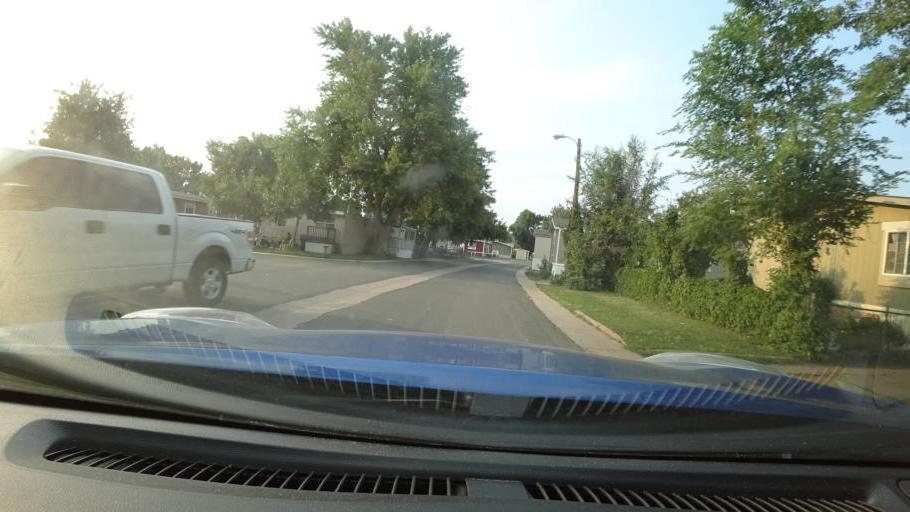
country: US
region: Colorado
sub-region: Adams County
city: Aurora
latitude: 39.7452
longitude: -104.7886
